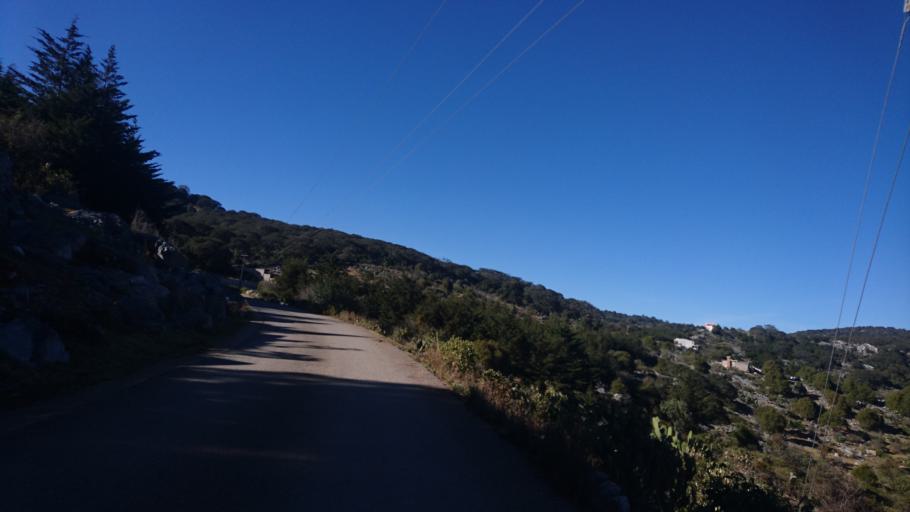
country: MX
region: San Luis Potosi
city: Zaragoza
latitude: 22.0231
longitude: -100.6017
